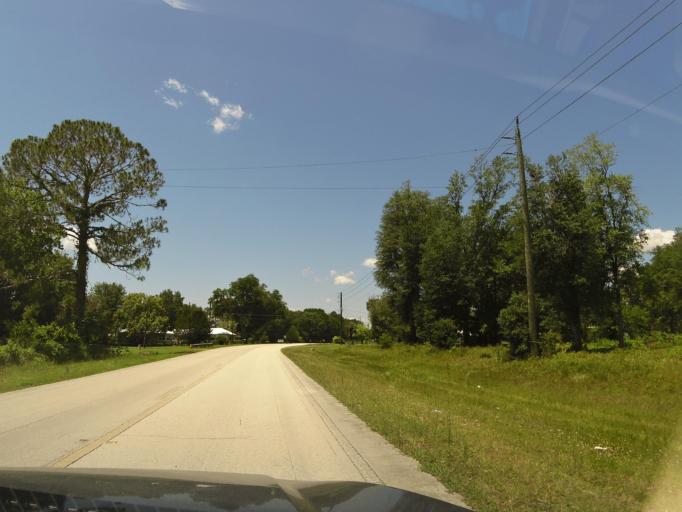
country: US
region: Florida
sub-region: Bradford County
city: Starke
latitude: 30.0448
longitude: -82.0918
